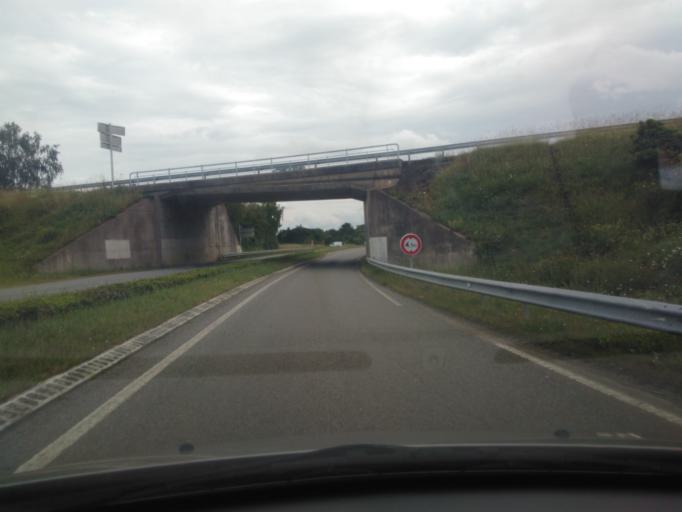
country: FR
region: Pays de la Loire
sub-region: Departement de la Loire-Atlantique
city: La Bernerie-en-Retz
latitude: 47.1044
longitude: -2.0496
